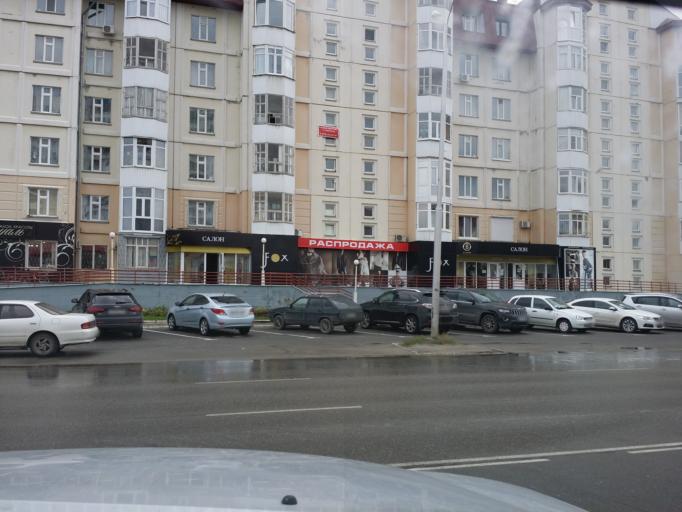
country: RU
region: Khanty-Mansiyskiy Avtonomnyy Okrug
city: Nizhnevartovsk
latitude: 60.9362
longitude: 76.5846
